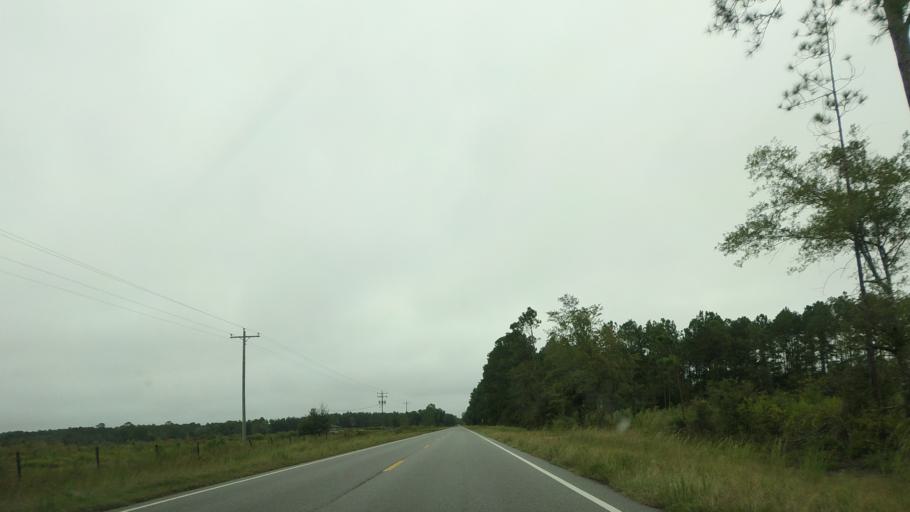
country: US
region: Georgia
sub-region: Berrien County
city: Enigma
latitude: 31.3647
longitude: -83.2269
